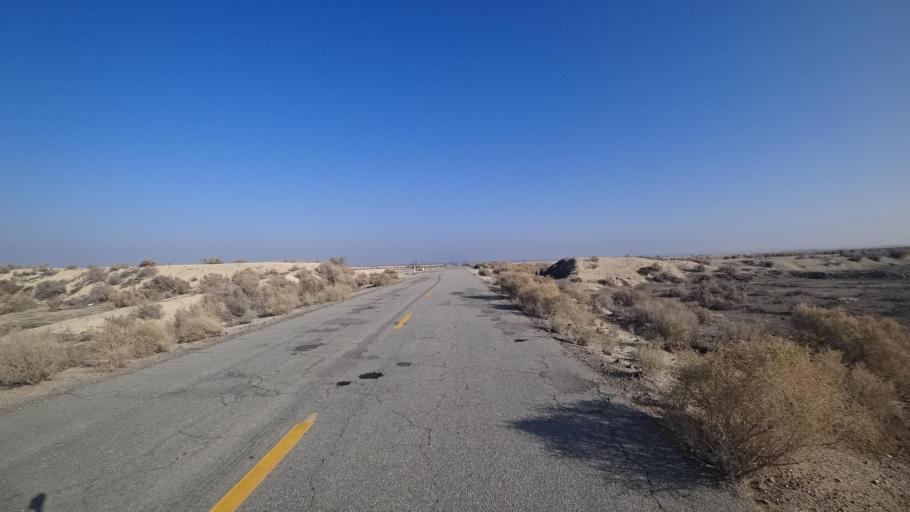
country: US
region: California
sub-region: Kern County
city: Maricopa
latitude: 35.1011
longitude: -119.3771
